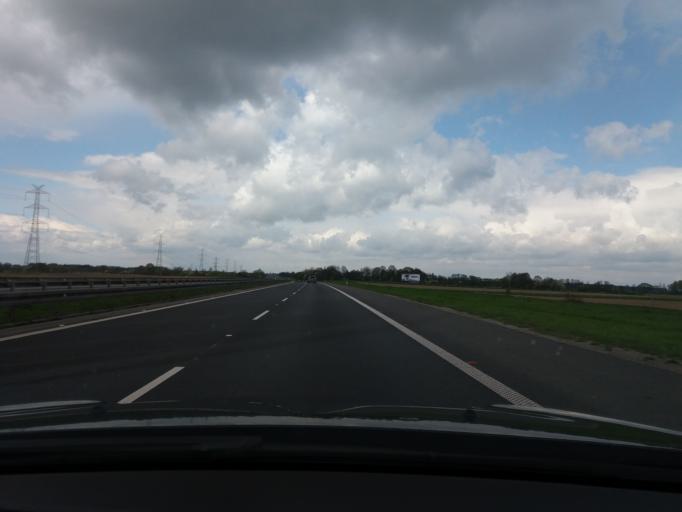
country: PL
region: Lower Silesian Voivodeship
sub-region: Powiat strzelinski
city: Wiazow
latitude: 50.8154
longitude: 17.3091
